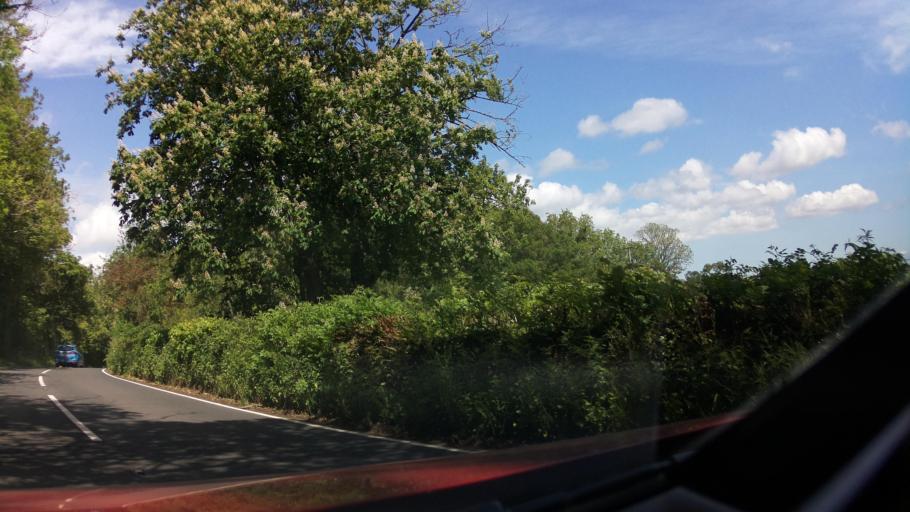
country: GB
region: Wales
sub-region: Monmouthshire
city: Mitchel Troy
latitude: 51.7715
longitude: -2.7331
